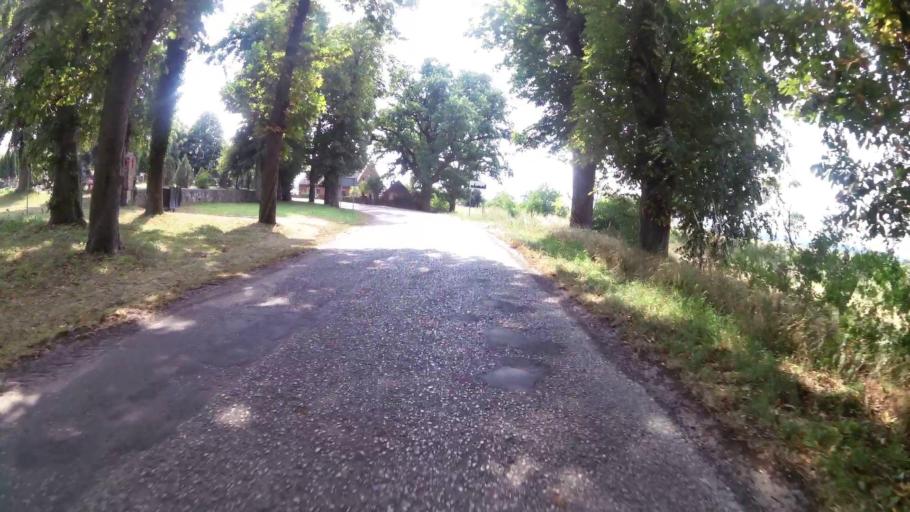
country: PL
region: West Pomeranian Voivodeship
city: Trzcinsko Zdroj
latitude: 52.8921
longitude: 14.5258
